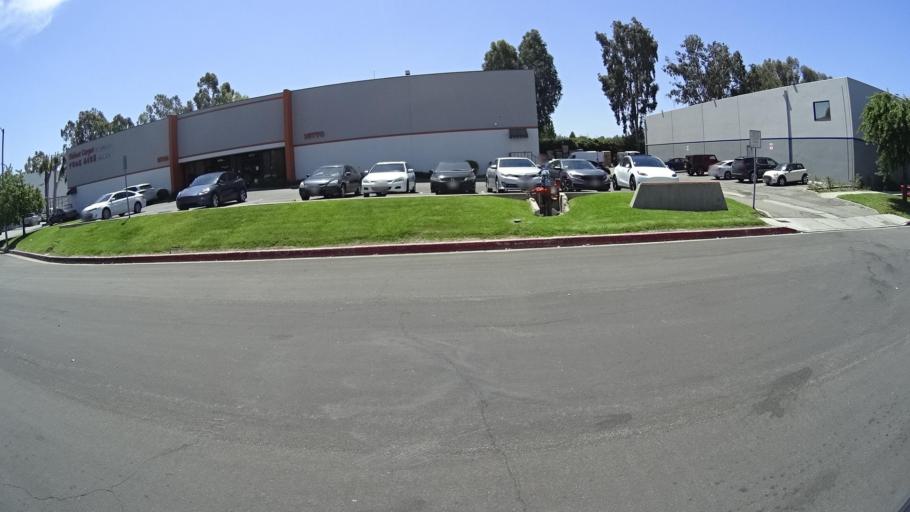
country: US
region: California
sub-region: Los Angeles County
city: La Puente
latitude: 34.0013
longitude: -117.9427
